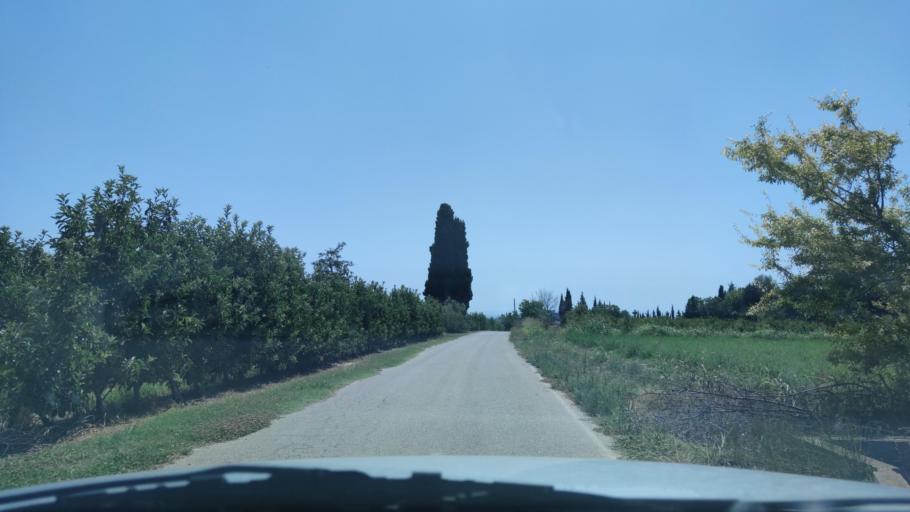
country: ES
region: Catalonia
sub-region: Provincia de Lleida
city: Lleida
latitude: 41.6389
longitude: 0.5956
